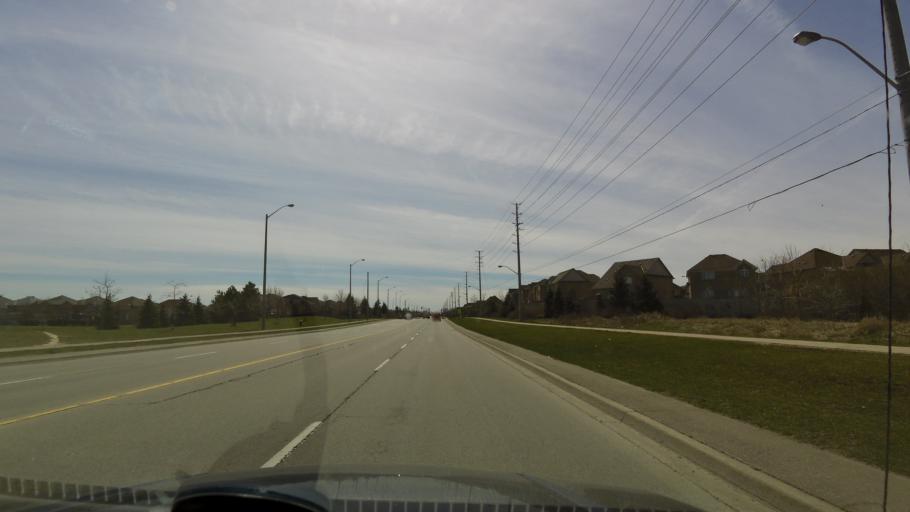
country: CA
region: Ontario
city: Brampton
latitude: 43.7203
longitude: -79.8197
